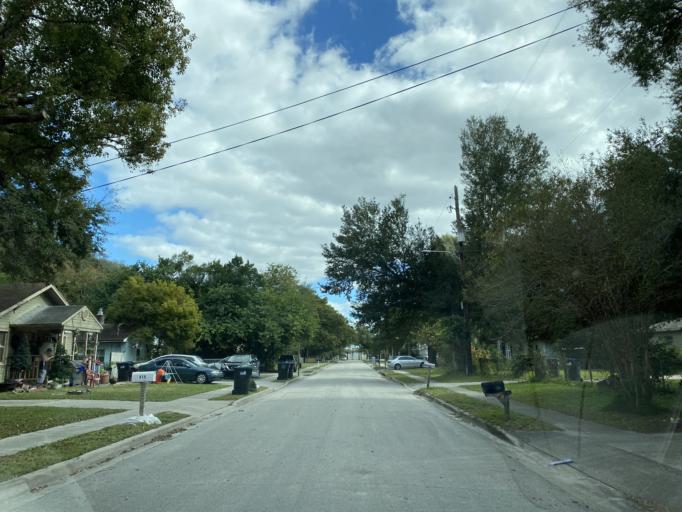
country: US
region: Florida
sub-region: Orange County
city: Holden Heights
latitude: 28.5164
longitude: -81.3924
